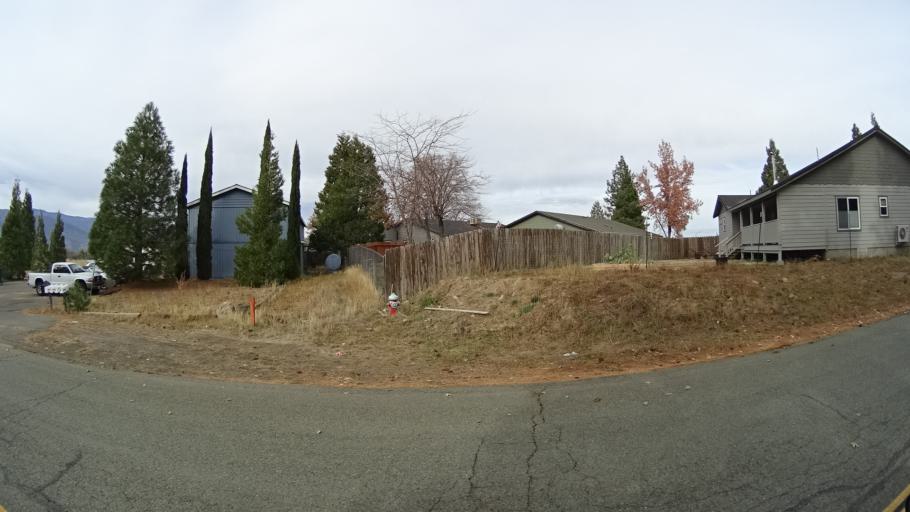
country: US
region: California
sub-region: Siskiyou County
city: Weed
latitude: 41.4294
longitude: -122.3809
